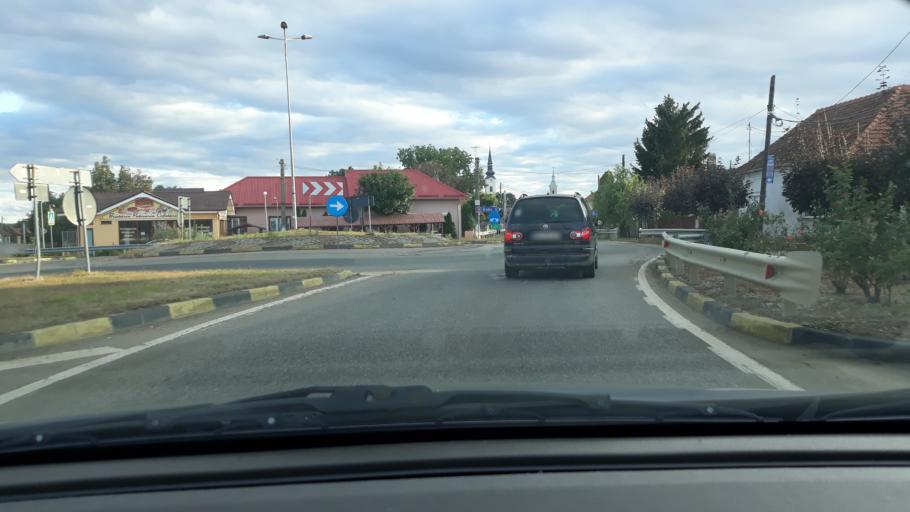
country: RO
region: Bihor
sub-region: Comuna Biharea
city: Biharea
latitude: 47.1573
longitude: 21.9222
